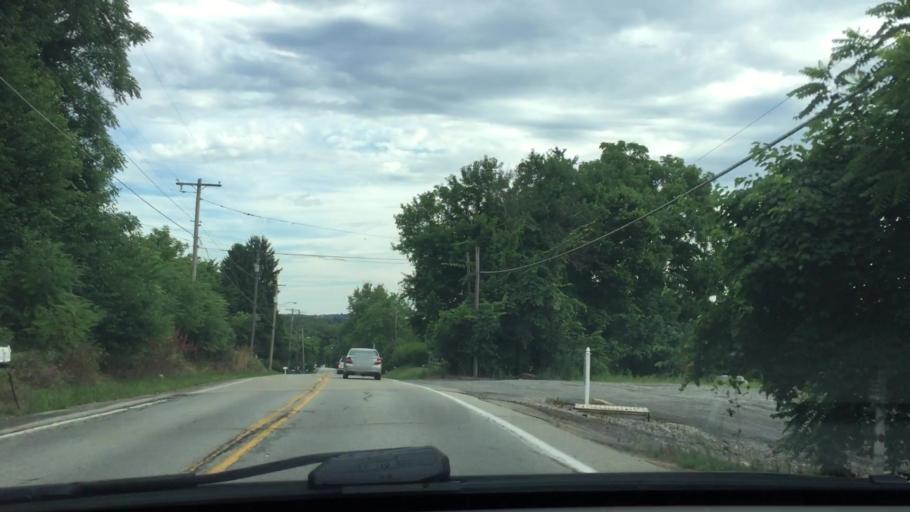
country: US
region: Pennsylvania
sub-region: Washington County
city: East Washington
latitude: 40.1976
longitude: -80.2369
